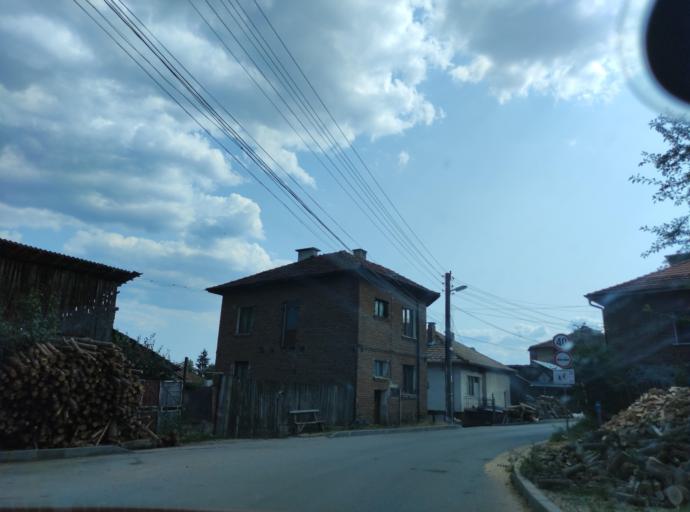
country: BG
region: Blagoevgrad
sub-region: Obshtina Belitsa
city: Belitsa
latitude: 41.9526
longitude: 23.5566
